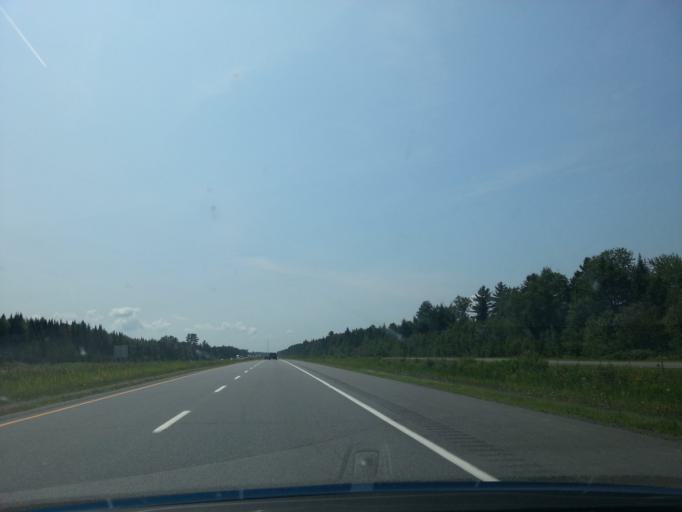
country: CA
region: Quebec
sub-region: Mauricie
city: Daveluyville
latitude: 46.2617
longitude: -72.0287
